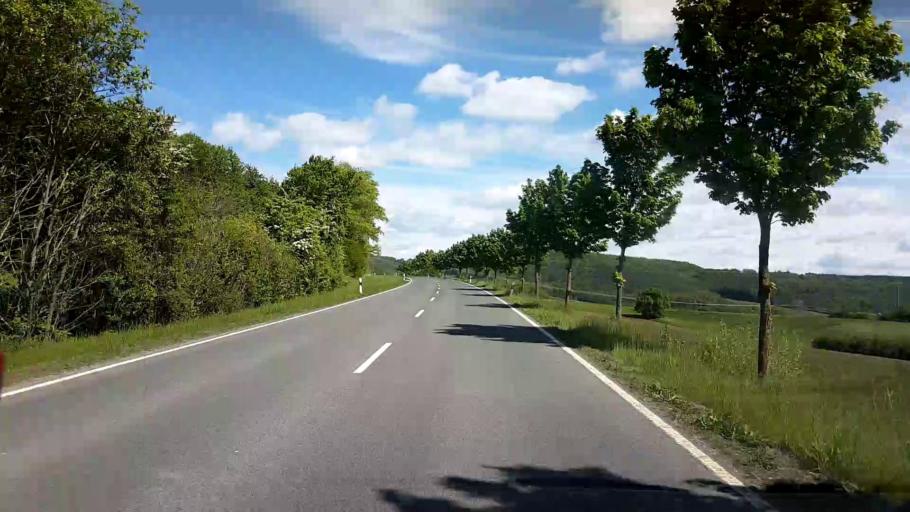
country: DE
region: Bavaria
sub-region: Upper Franconia
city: Eggolsheim
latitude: 49.8061
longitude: 11.0947
